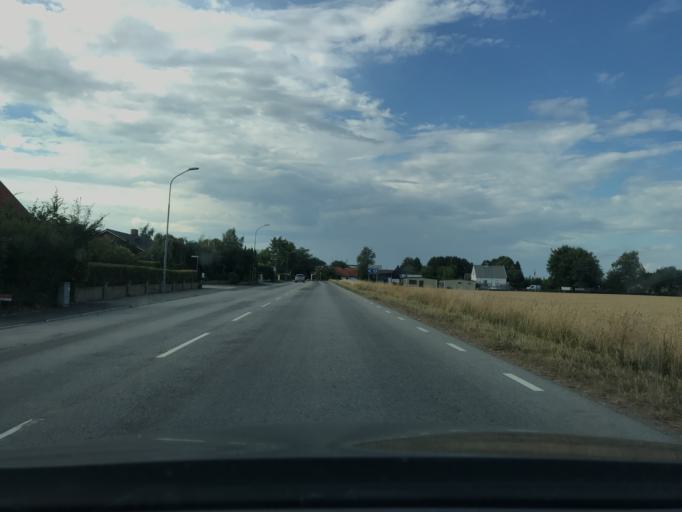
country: SE
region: Skane
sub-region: Simrishamns Kommun
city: Simrishamn
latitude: 55.4998
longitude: 14.1622
